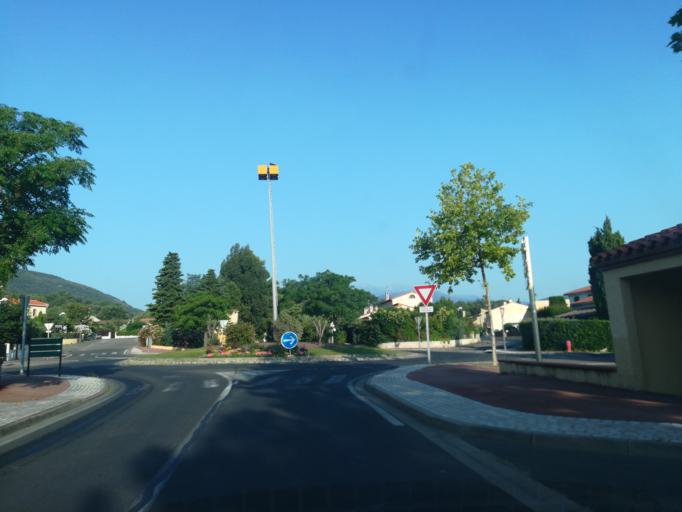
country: FR
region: Languedoc-Roussillon
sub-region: Departement des Pyrenees-Orientales
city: Ceret
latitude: 42.4845
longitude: 2.7614
